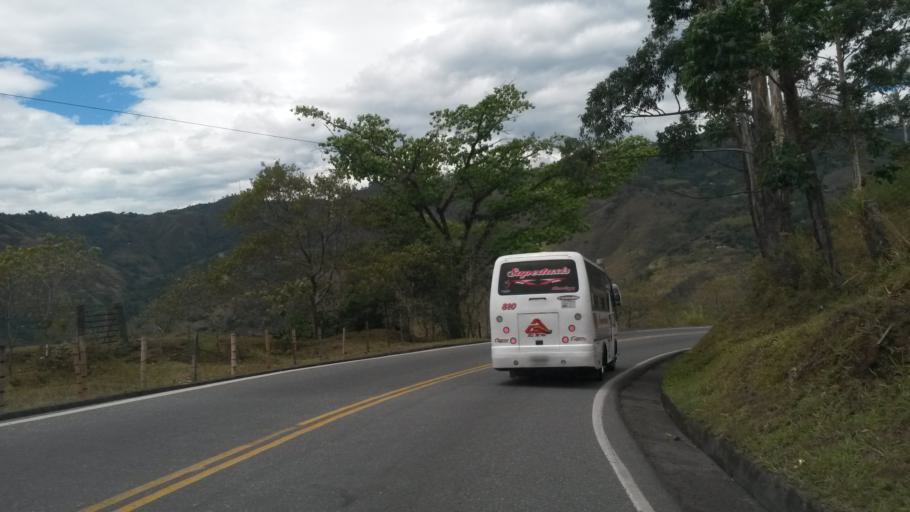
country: CO
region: Cauca
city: Rosas
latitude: 2.2811
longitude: -76.7216
